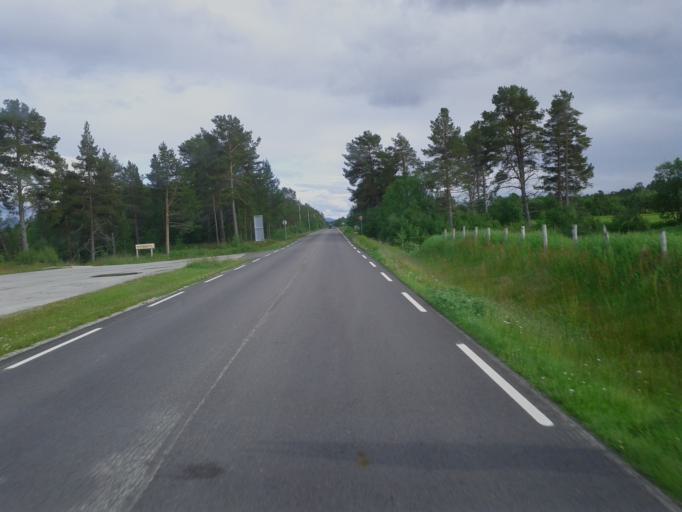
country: NO
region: Sor-Trondelag
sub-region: Roros
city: Roros
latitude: 62.2860
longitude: 11.7352
